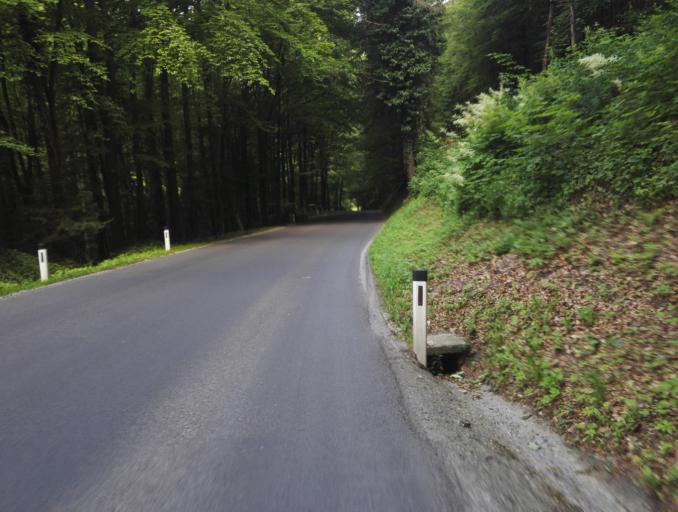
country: AT
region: Styria
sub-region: Politischer Bezirk Graz-Umgebung
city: Gratwein
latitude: 47.0904
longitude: 15.3154
